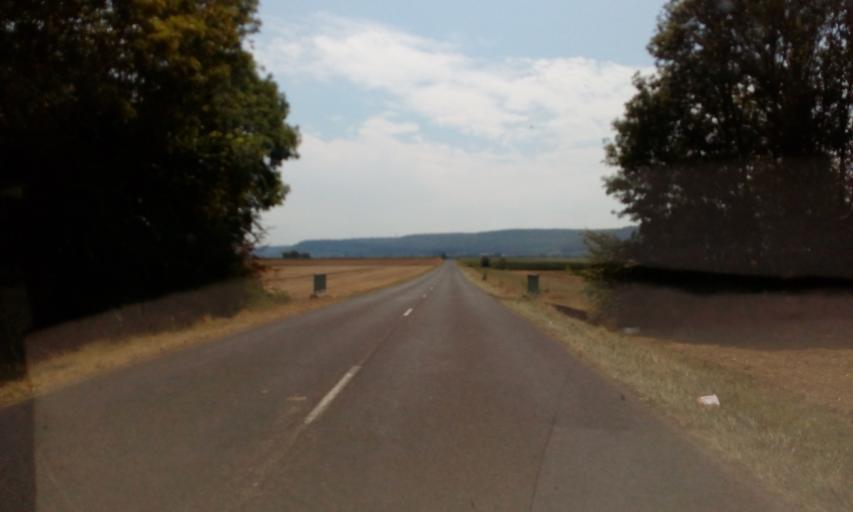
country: FR
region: Lorraine
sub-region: Departement de la Meuse
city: Vigneulles-les-Hattonchatel
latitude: 49.0620
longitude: 5.6479
